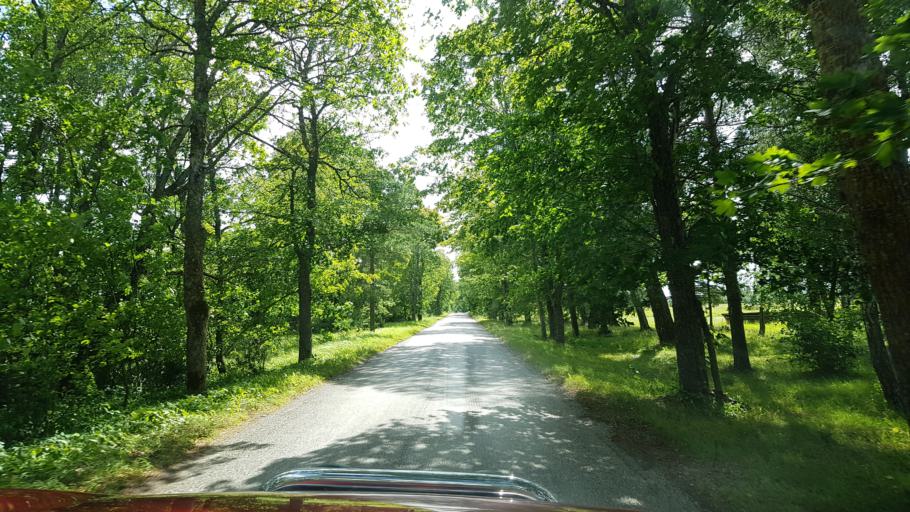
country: EE
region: Laeaene
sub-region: Lihula vald
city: Lihula
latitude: 58.5891
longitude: 23.5373
